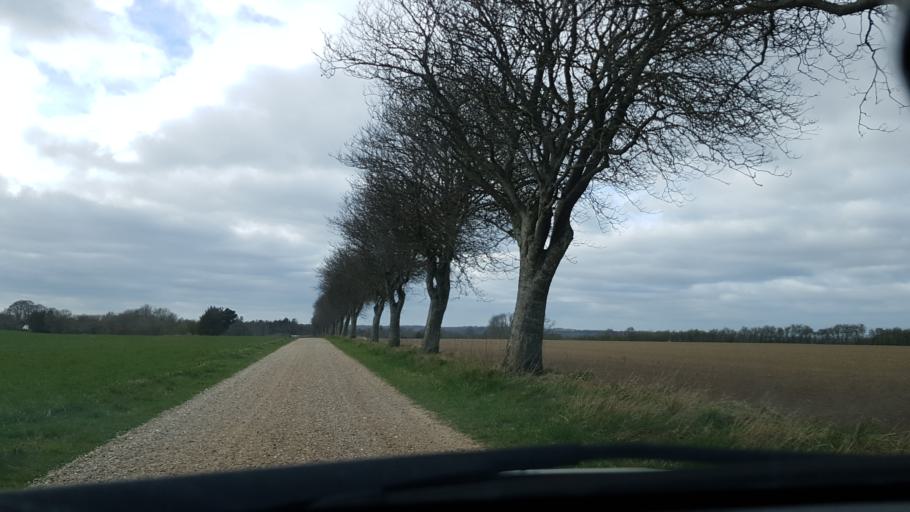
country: DK
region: South Denmark
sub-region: Vejen Kommune
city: Brorup
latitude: 55.4250
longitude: 9.0249
